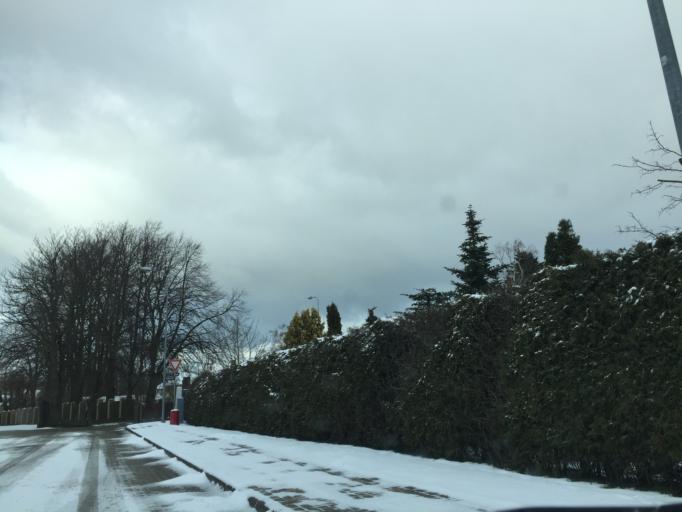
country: LV
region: Ventspils
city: Ventspils
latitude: 57.3858
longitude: 21.5646
